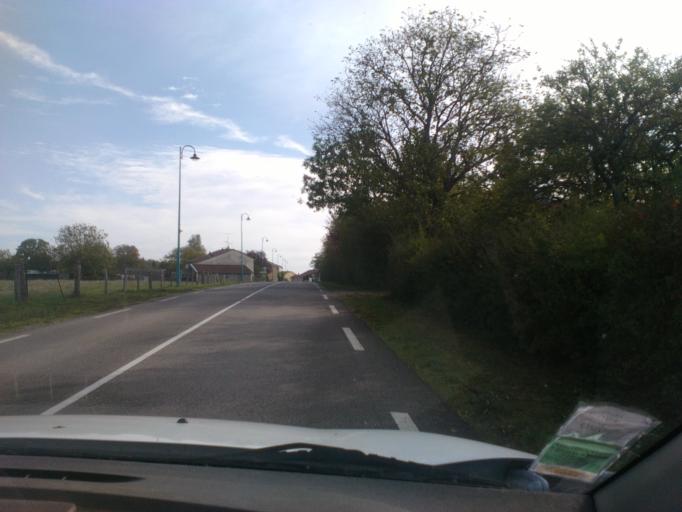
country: FR
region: Lorraine
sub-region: Departement des Vosges
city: Rambervillers
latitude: 48.3499
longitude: 6.5327
